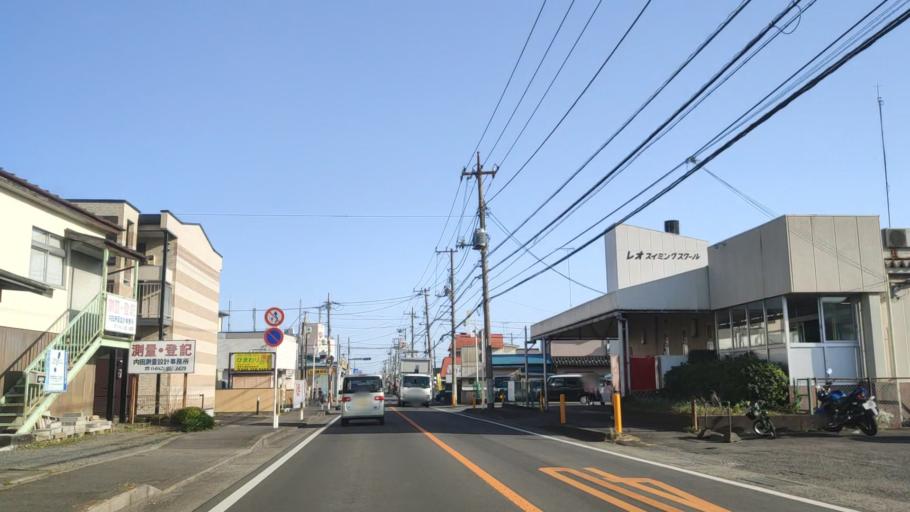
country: JP
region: Kanagawa
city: Zama
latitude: 35.5188
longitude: 139.3318
